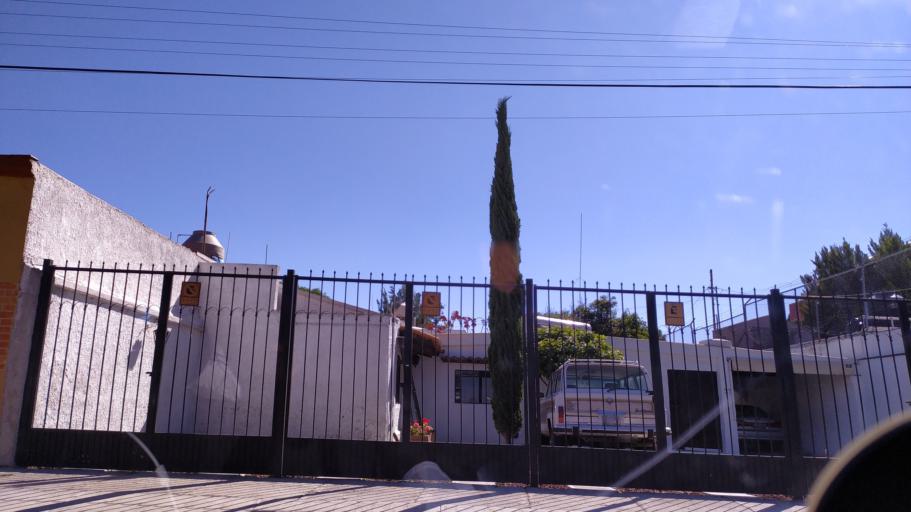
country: MX
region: Jalisco
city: Guadalajara
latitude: 20.6746
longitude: -103.4474
